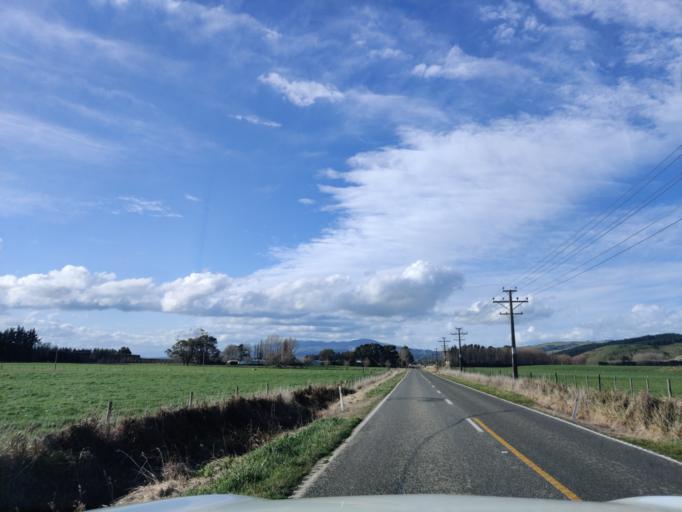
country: NZ
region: Manawatu-Wanganui
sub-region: Palmerston North City
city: Palmerston North
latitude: -40.3420
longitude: 175.7154
